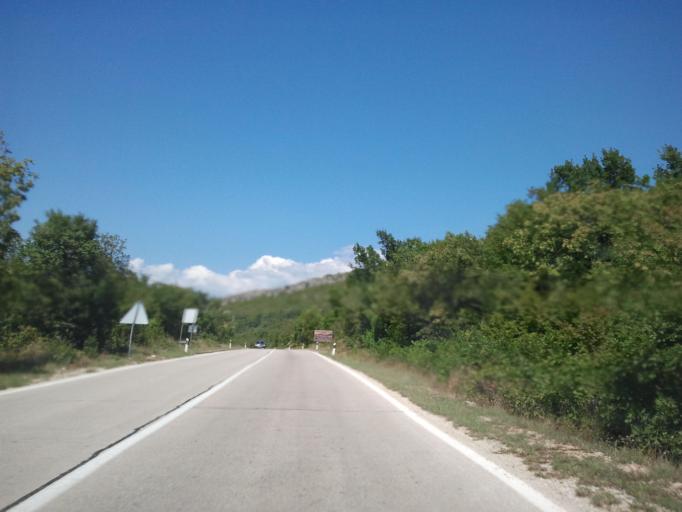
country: HR
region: Zadarska
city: Krusevo
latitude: 44.1655
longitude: 15.6264
